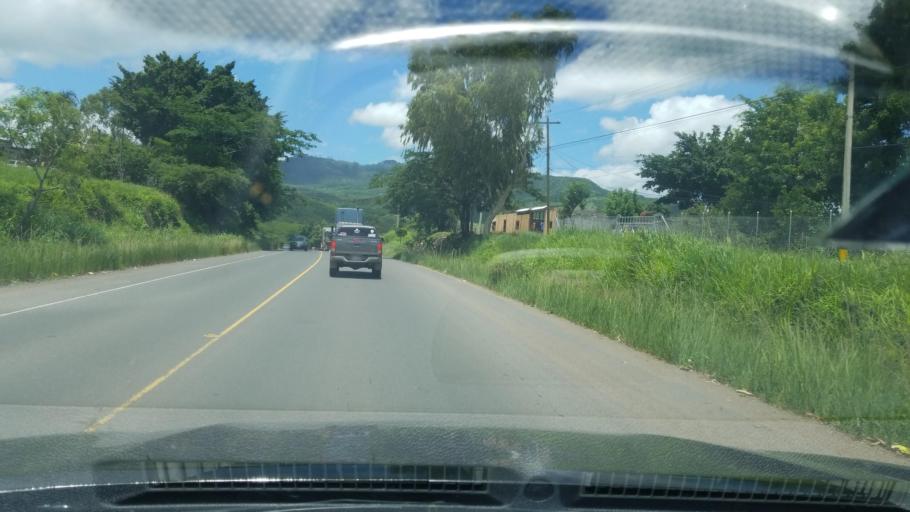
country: HN
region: Francisco Morazan
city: Cofradia
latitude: 14.2602
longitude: -87.2452
